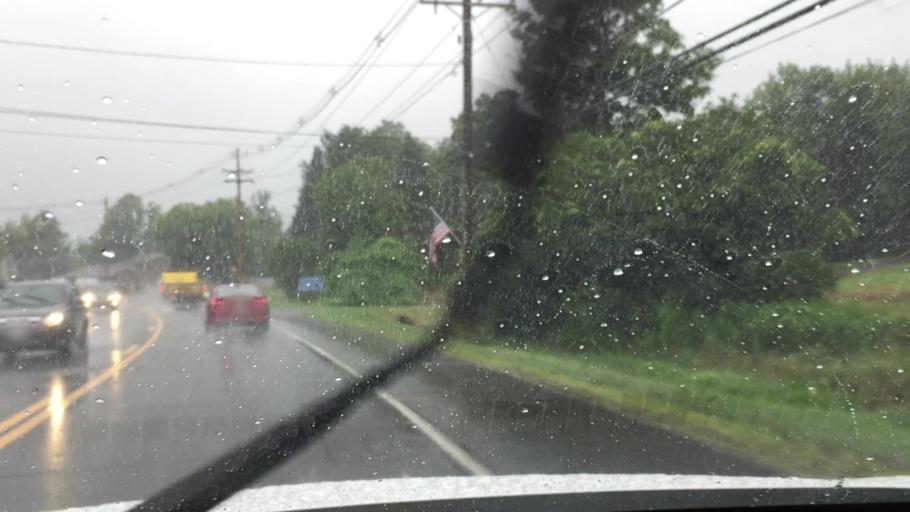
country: US
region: Massachusetts
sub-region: Berkshire County
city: Lanesborough
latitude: 42.5361
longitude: -73.2293
